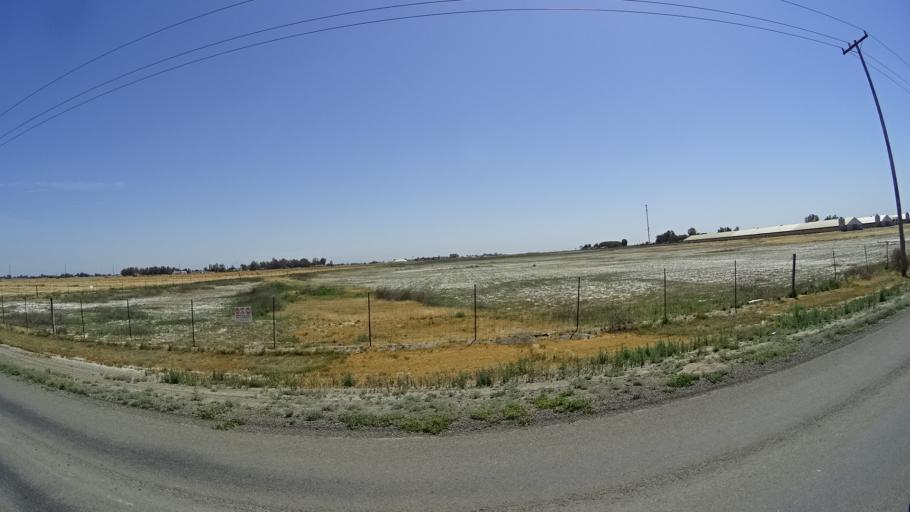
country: US
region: California
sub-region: Kings County
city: Stratford
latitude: 36.2361
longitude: -119.7984
